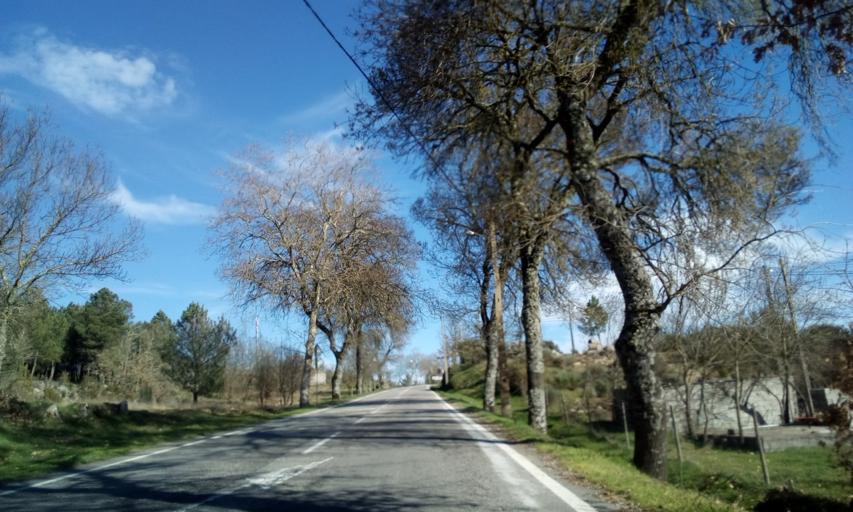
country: PT
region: Guarda
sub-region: Guarda
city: Sequeira
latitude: 40.5795
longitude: -7.1723
